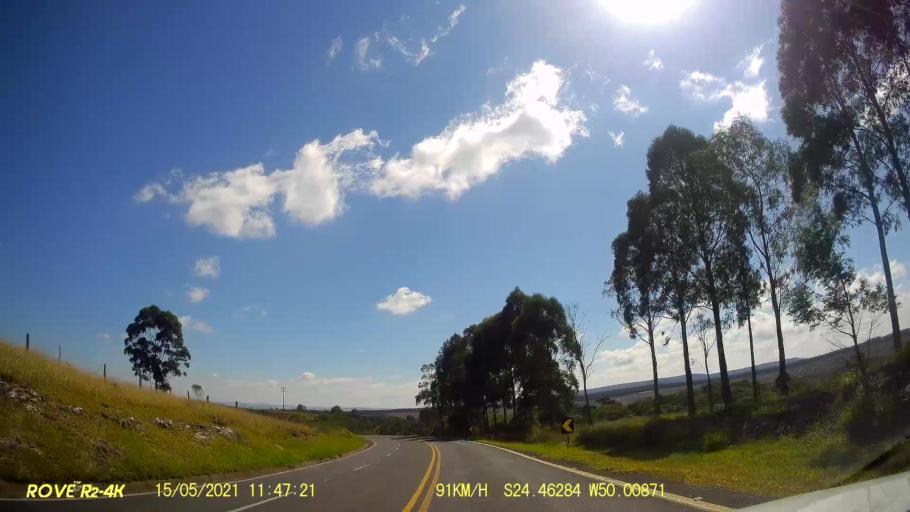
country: BR
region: Parana
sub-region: Pirai Do Sul
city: Pirai do Sul
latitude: -24.4628
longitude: -50.0087
